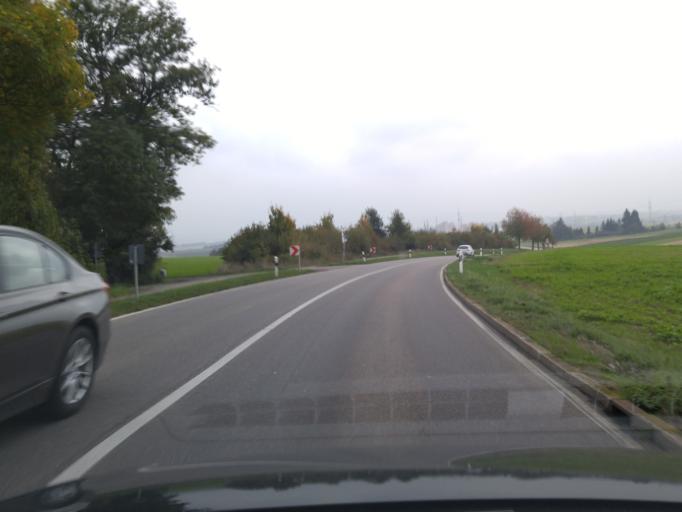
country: DE
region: Baden-Wuerttemberg
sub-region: Regierungsbezirk Stuttgart
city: Leingarten
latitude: 49.1738
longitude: 9.1514
